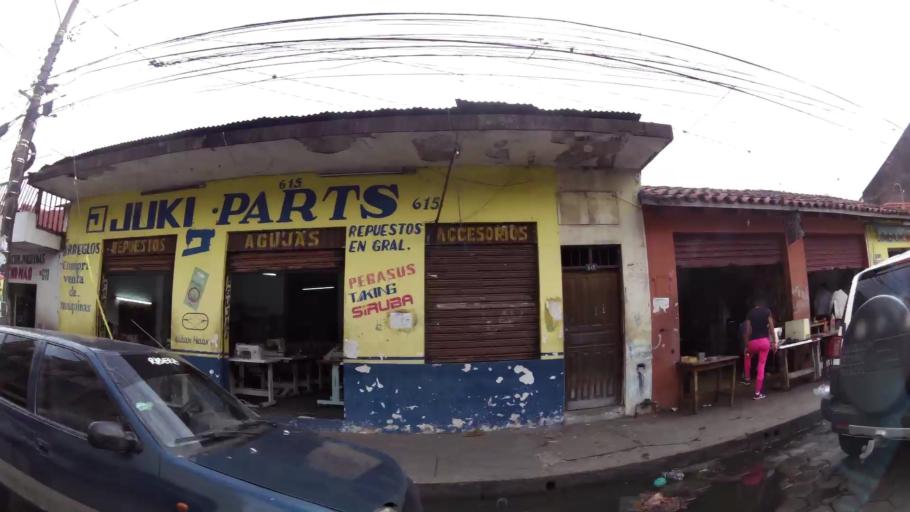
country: BO
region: Santa Cruz
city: Santa Cruz de la Sierra
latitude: -17.7766
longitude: -63.1785
